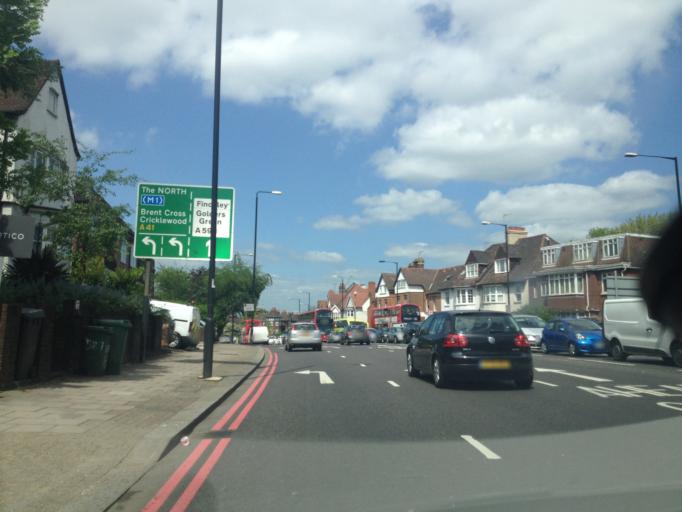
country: GB
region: England
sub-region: Greater London
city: Belsize Park
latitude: 51.5580
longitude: -0.1959
